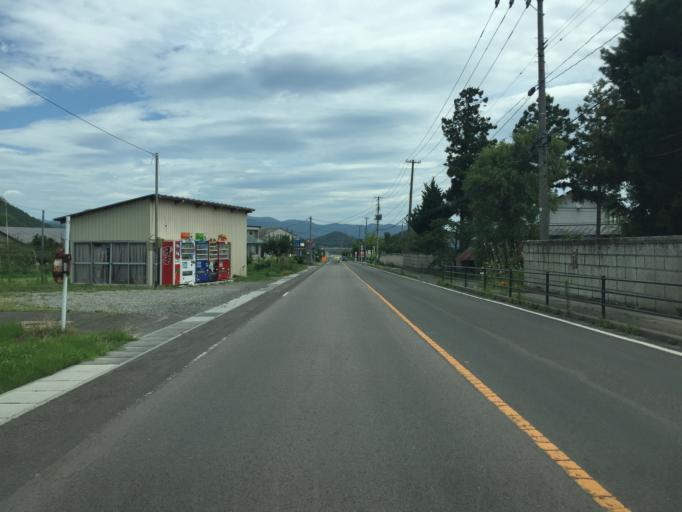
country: JP
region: Fukushima
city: Fukushima-shi
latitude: 37.8004
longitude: 140.4041
